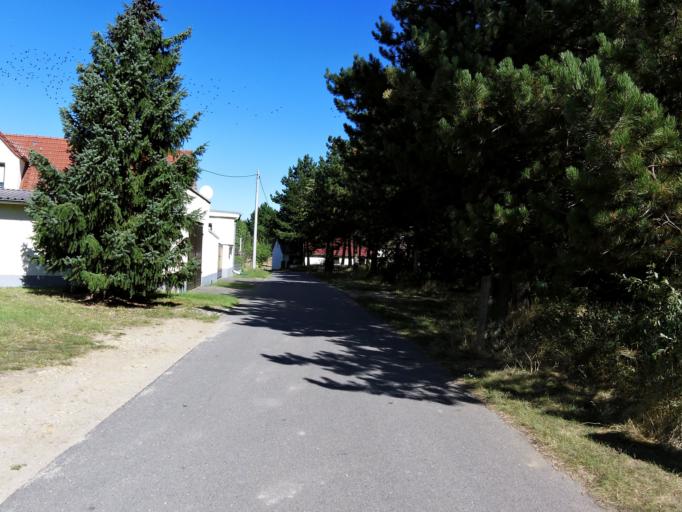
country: DE
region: Saxony-Anhalt
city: Pretzsch
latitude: 51.6999
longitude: 12.8254
